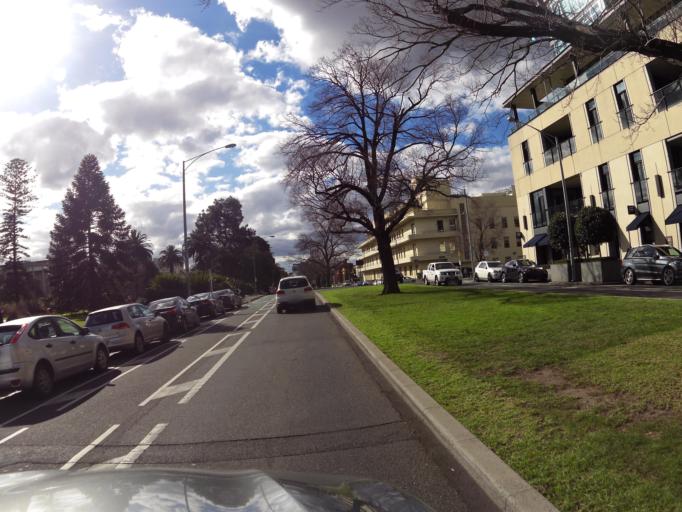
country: AU
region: Victoria
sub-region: Melbourne
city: East Melbourne
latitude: -37.8121
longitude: 144.9832
